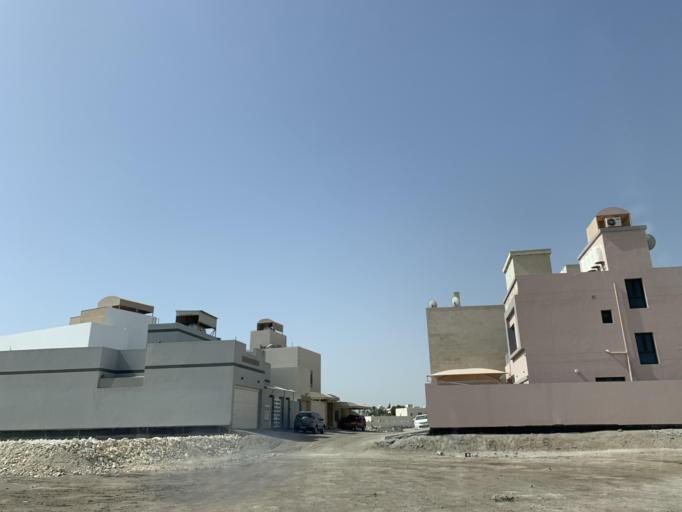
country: BH
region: Northern
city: Sitrah
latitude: 26.1506
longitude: 50.6017
